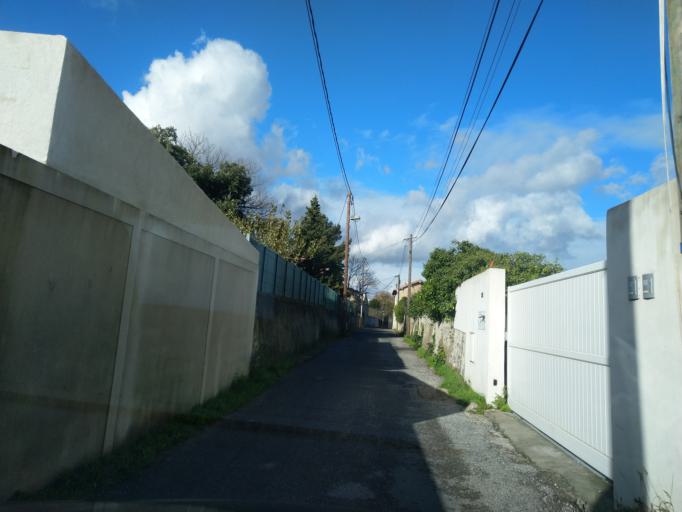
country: FR
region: Provence-Alpes-Cote d'Azur
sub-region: Departement des Bouches-du-Rhone
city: Marseille 12
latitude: 43.3114
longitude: 5.4344
